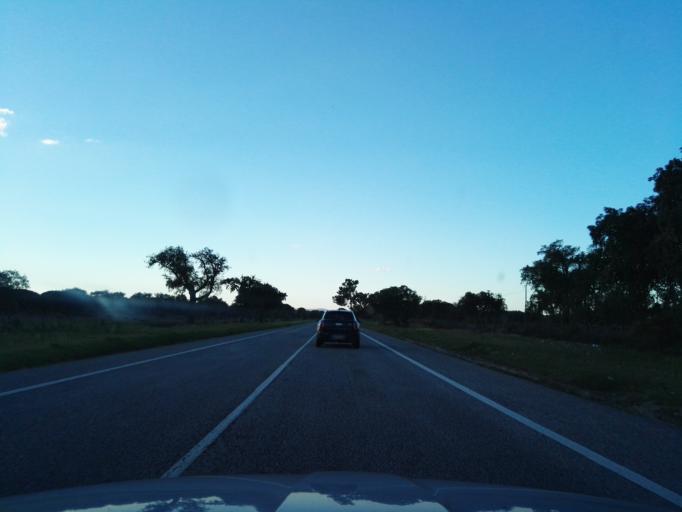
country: PT
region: Santarem
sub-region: Benavente
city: Poceirao
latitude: 38.8872
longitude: -8.8240
